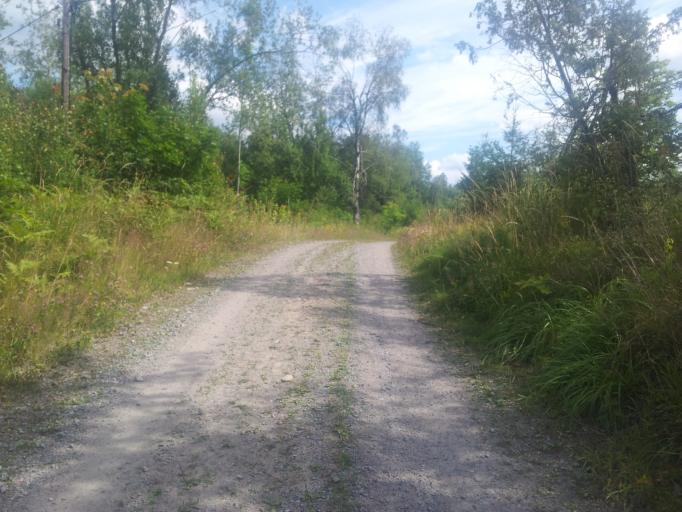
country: SE
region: Stockholm
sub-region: Norrtalje Kommun
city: Nykvarn
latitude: 59.8950
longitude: 18.2439
